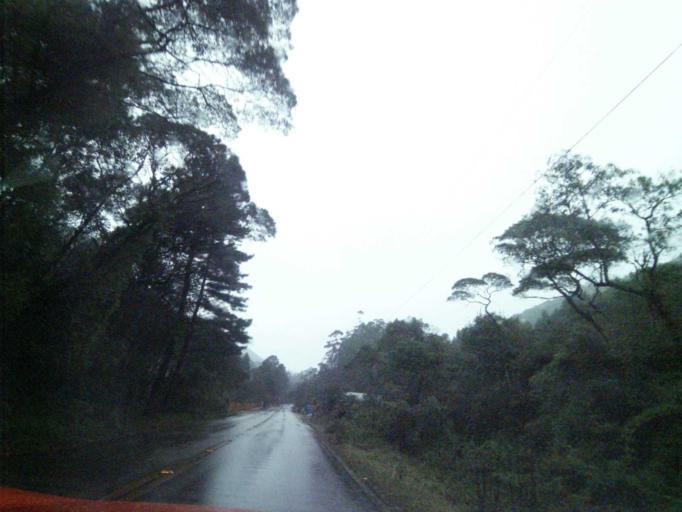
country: BR
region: Santa Catarina
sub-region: Anitapolis
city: Anitapolis
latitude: -27.7856
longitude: -49.0430
